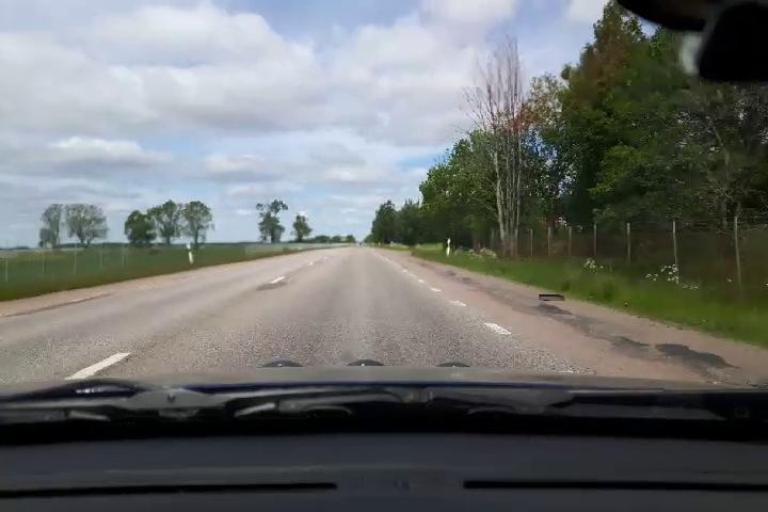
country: SE
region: Uppsala
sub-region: Uppsala Kommun
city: Gamla Uppsala
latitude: 59.8913
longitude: 17.6168
